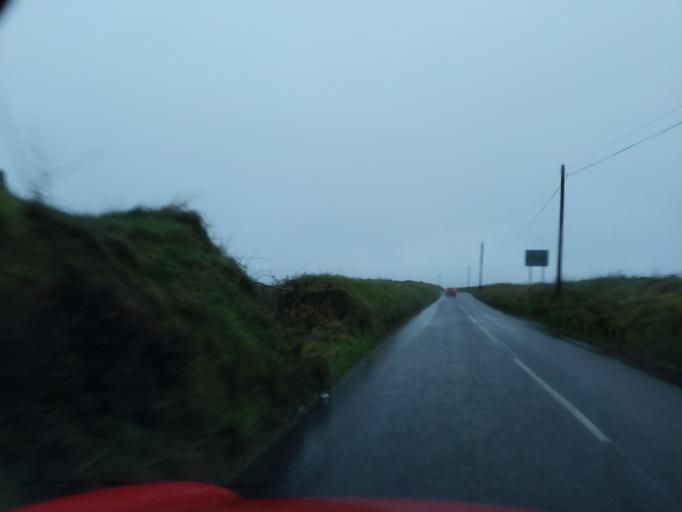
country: GB
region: England
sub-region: Cornwall
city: Camelford
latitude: 50.6408
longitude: -4.6945
